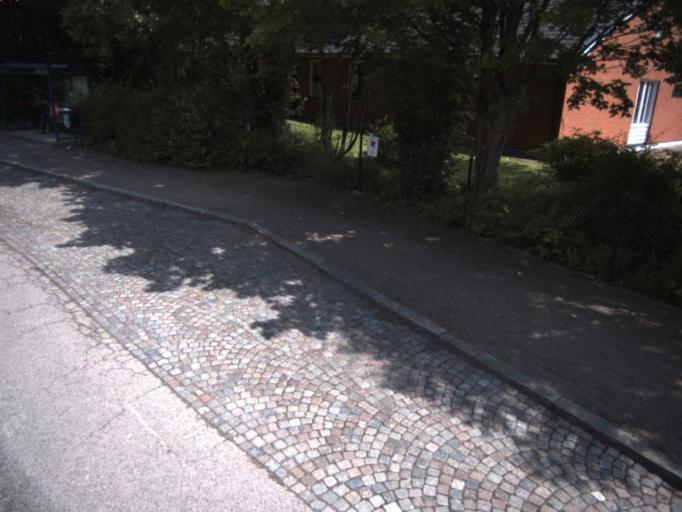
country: SE
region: Skane
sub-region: Helsingborg
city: Odakra
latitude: 56.0610
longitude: 12.7331
